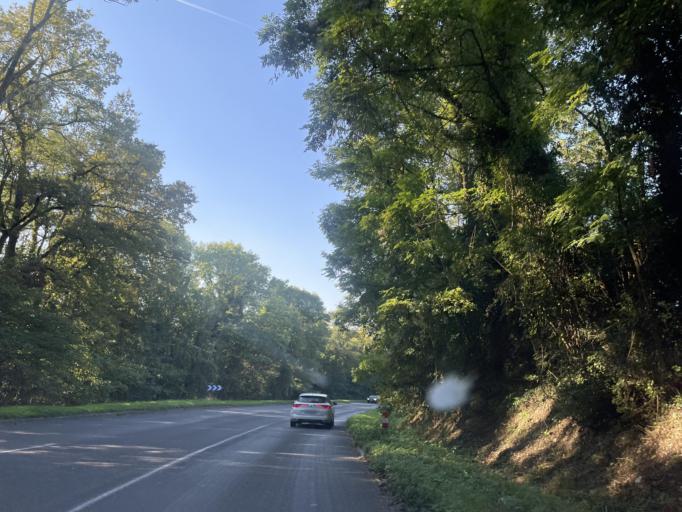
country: FR
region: Ile-de-France
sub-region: Departement de Seine-et-Marne
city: La Chapelle-sur-Crecy
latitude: 48.8508
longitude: 2.9337
